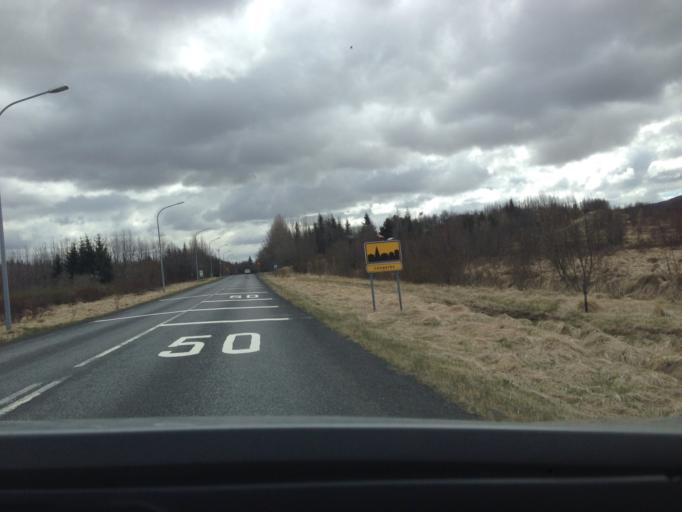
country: IS
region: South
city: Selfoss
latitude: 64.1204
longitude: -20.5034
